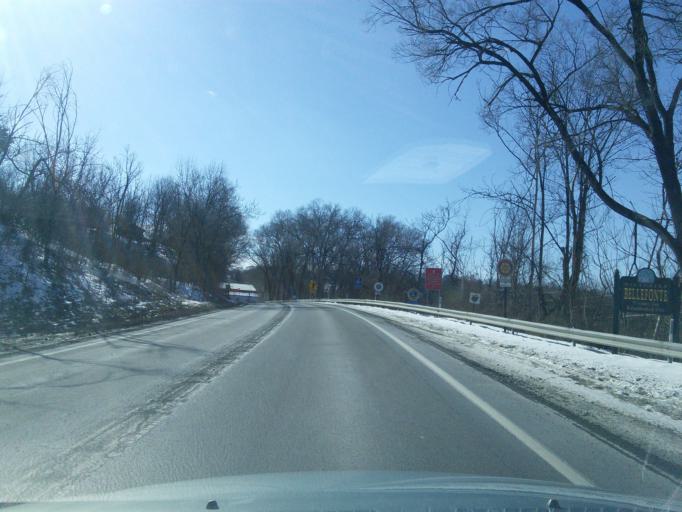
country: US
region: Pennsylvania
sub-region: Centre County
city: Bellefonte
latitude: 40.9190
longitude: -77.7857
